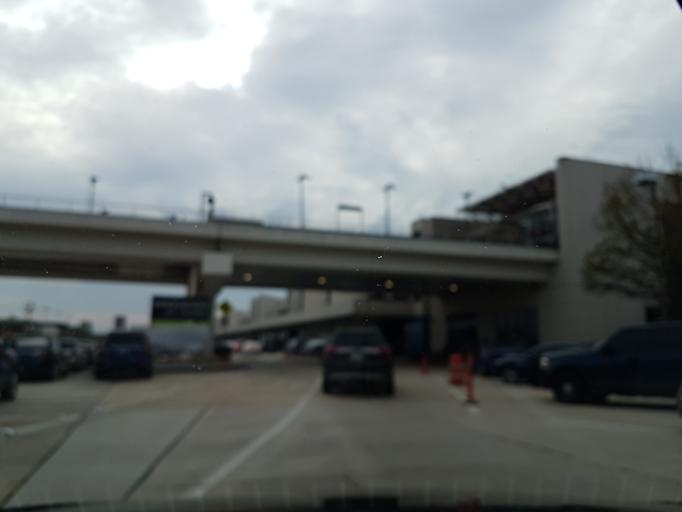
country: US
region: Georgia
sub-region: Fulton County
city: College Park
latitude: 33.6417
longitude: -84.4467
